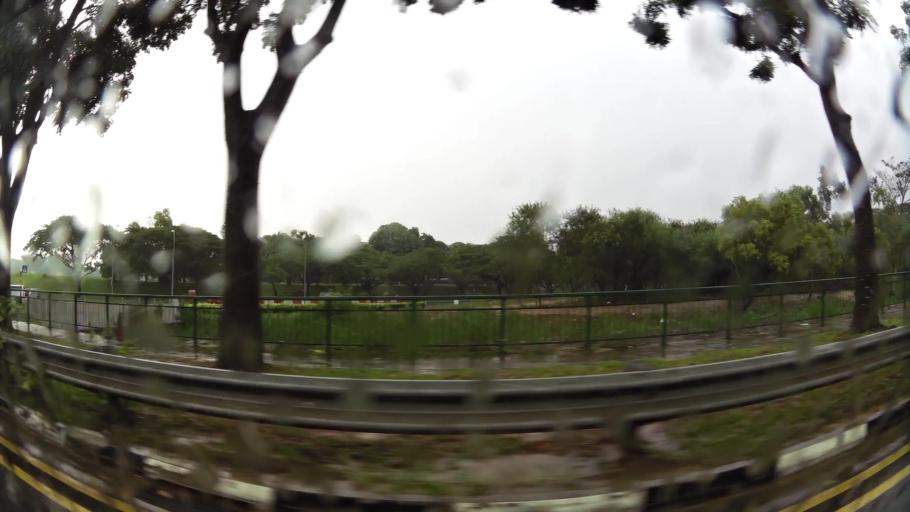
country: SG
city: Singapore
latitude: 1.3695
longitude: 103.9312
